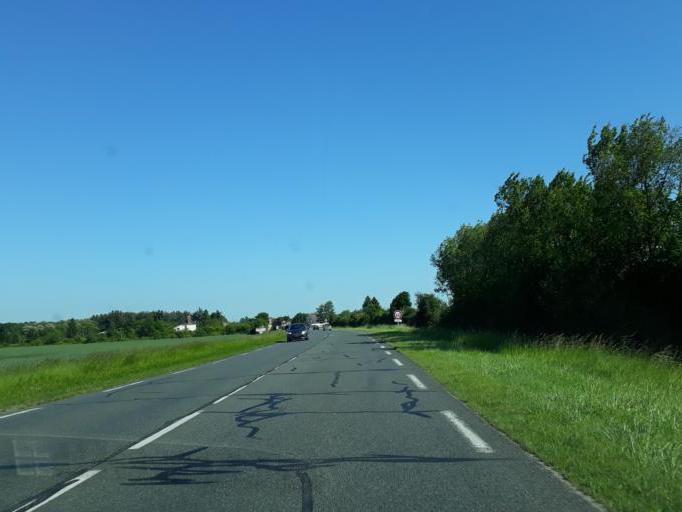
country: FR
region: Centre
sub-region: Departement du Loiret
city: Briare
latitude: 47.6000
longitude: 2.7873
